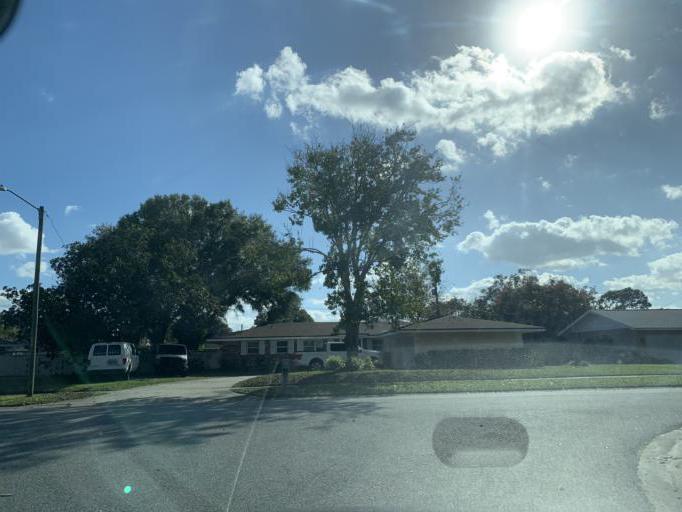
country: US
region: Florida
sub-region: Orange County
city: Eatonville
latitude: 28.6125
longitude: -81.3993
